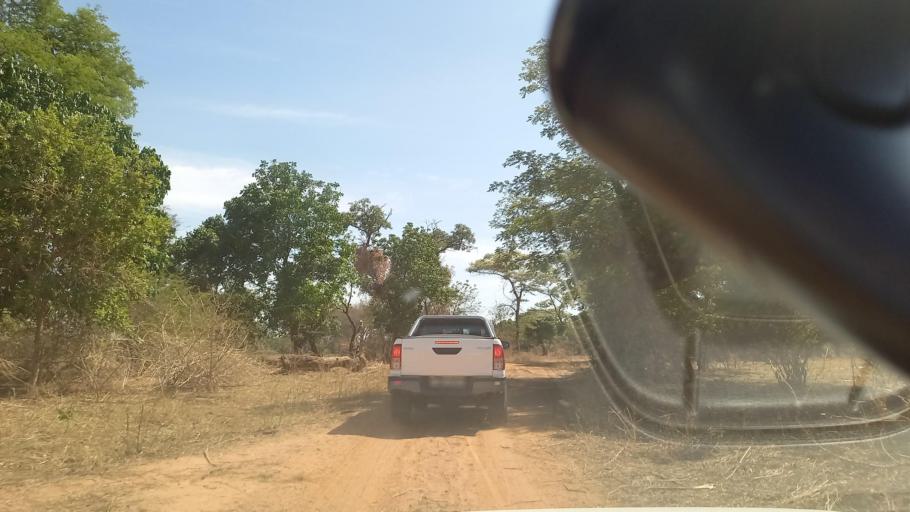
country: ZM
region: Southern
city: Mazabuka
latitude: -16.0328
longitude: 27.6238
